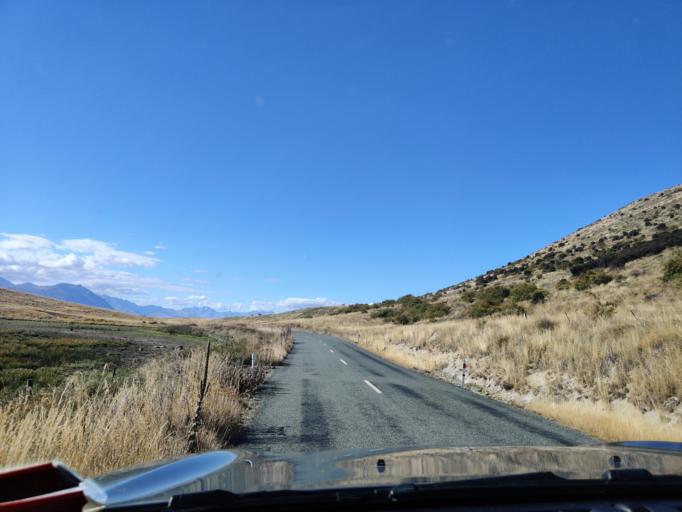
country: NZ
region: Canterbury
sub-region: Timaru District
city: Pleasant Point
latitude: -43.9784
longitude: 170.4631
